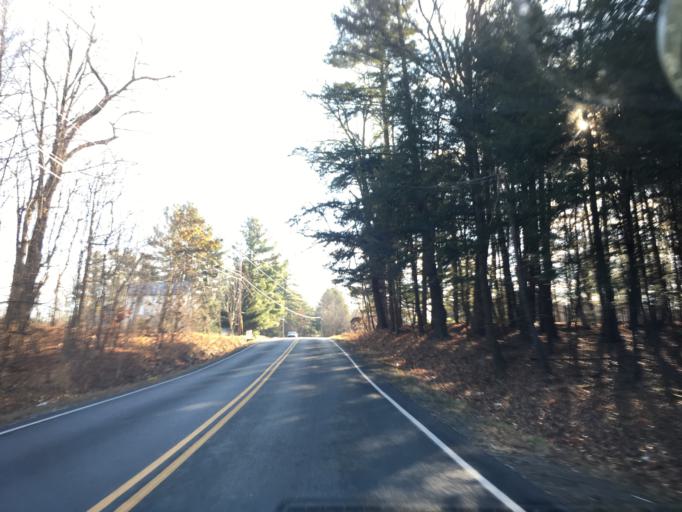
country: US
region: New York
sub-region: Rensselaer County
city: West Sand Lake
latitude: 42.6009
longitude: -73.6008
